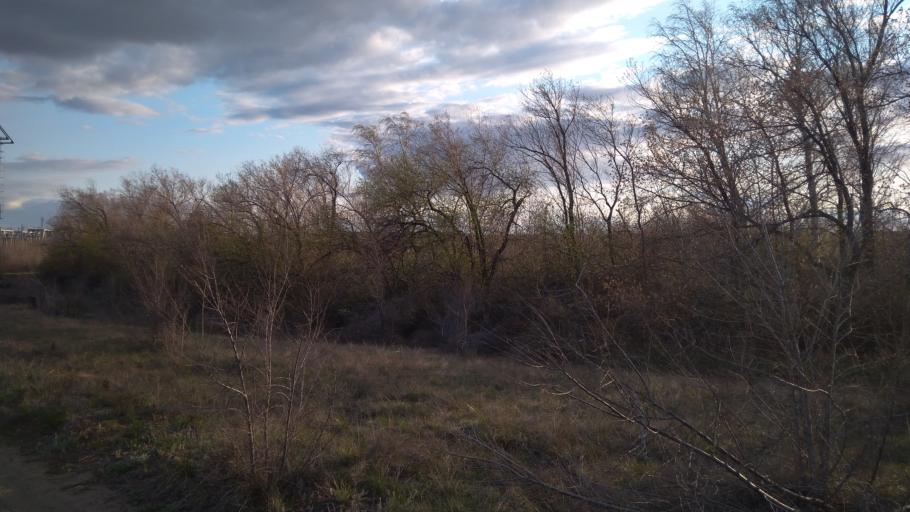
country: RU
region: Chelyabinsk
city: Troitsk
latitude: 54.0592
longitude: 61.6135
